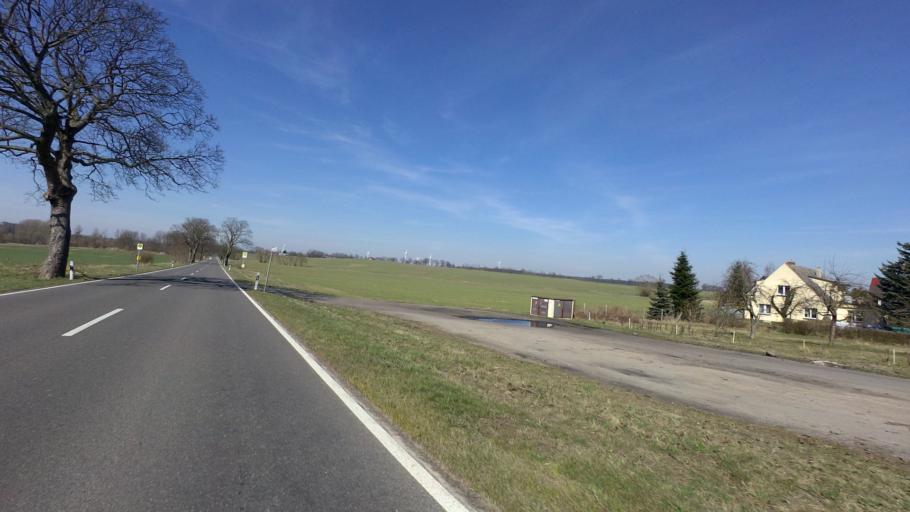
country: DE
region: Brandenburg
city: Protzel
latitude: 52.6193
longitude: 14.0184
